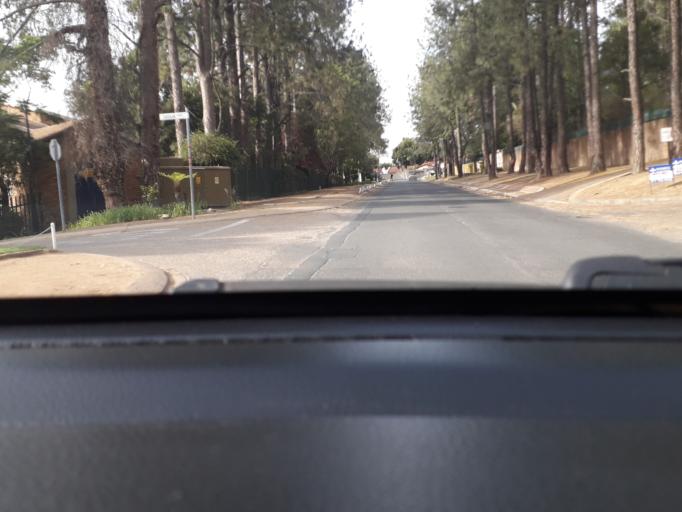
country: ZA
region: Gauteng
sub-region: City of Johannesburg Metropolitan Municipality
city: Diepsloot
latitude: -26.0387
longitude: 28.0309
